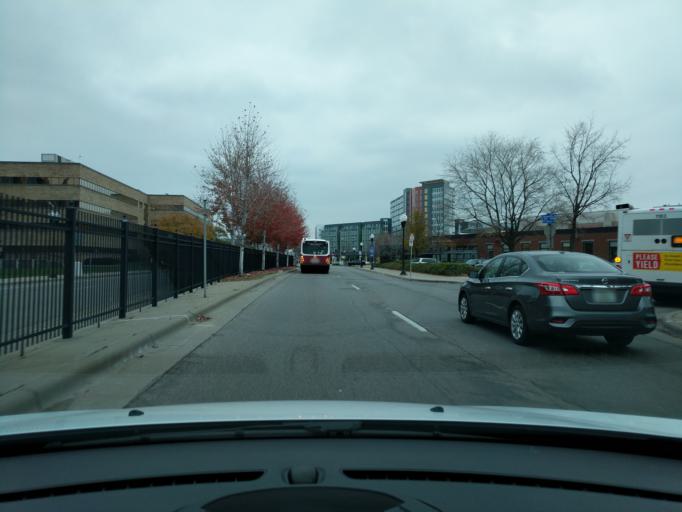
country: US
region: Minnesota
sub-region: Ramsey County
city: Lauderdale
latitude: 44.9752
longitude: -93.2259
